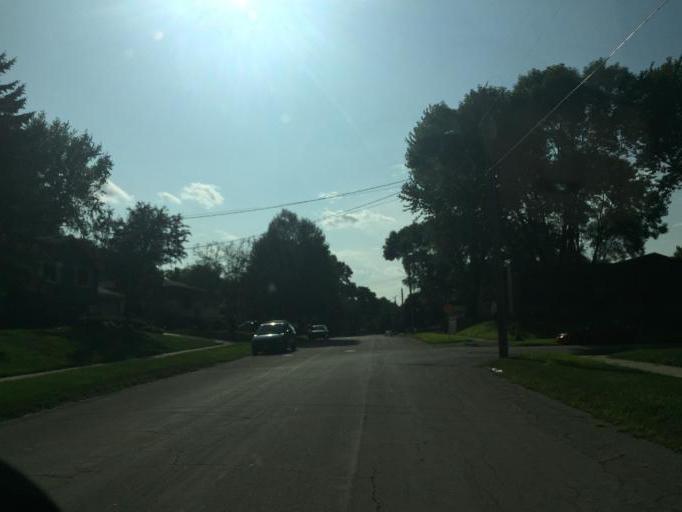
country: US
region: Minnesota
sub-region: Olmsted County
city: Rochester
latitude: 44.0447
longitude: -92.4960
